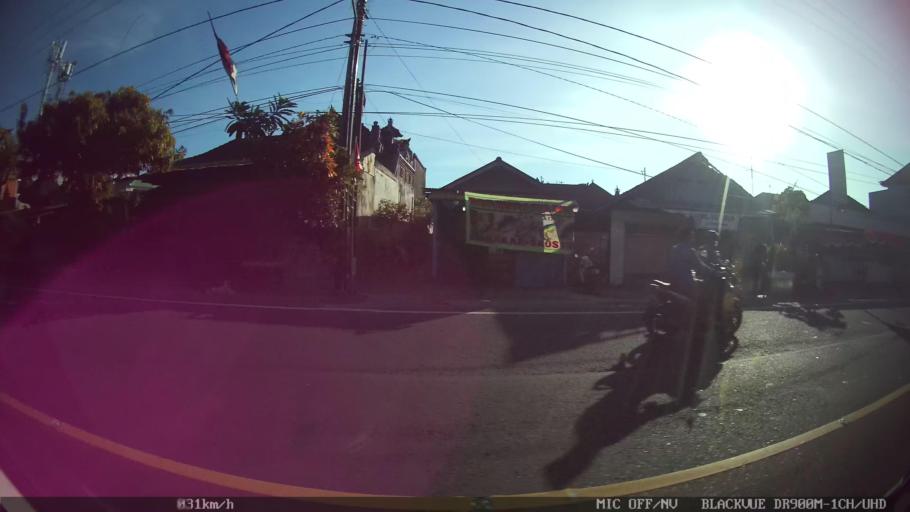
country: ID
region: Bali
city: Banjar Kertasari
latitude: -8.6317
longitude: 115.2017
